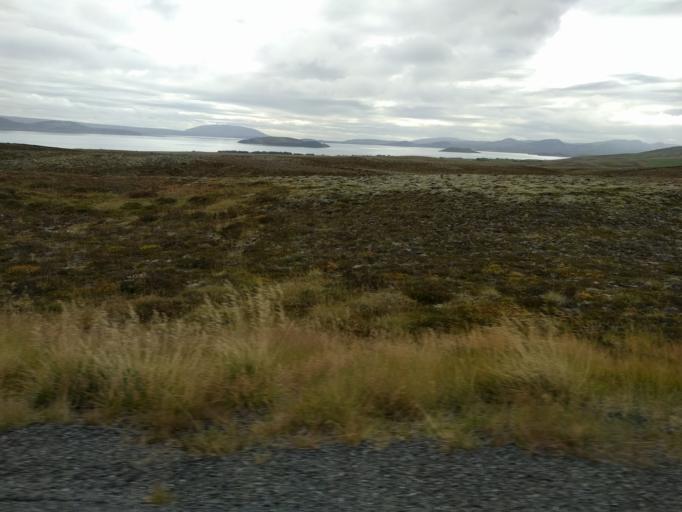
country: IS
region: South
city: Hveragerdi
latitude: 64.2196
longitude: -21.2342
